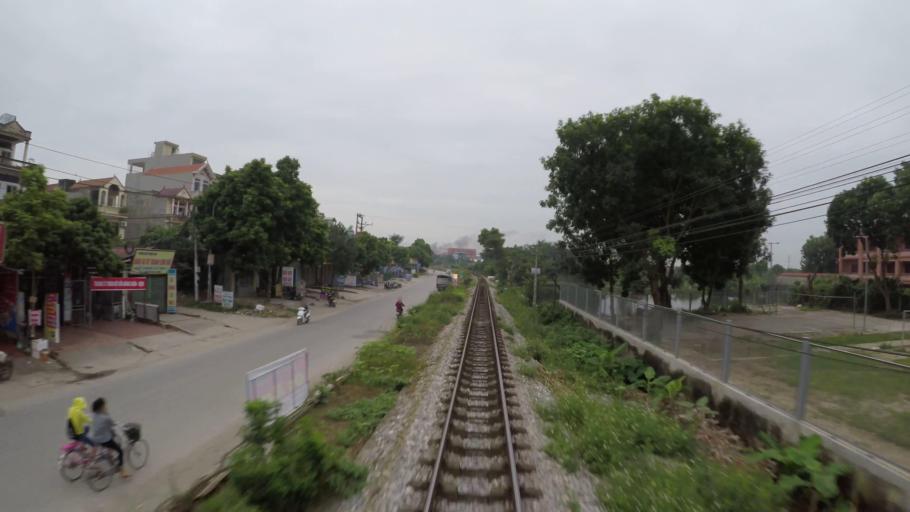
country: VN
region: Hung Yen
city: Nhu Quynh
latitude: 20.9785
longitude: 106.0146
